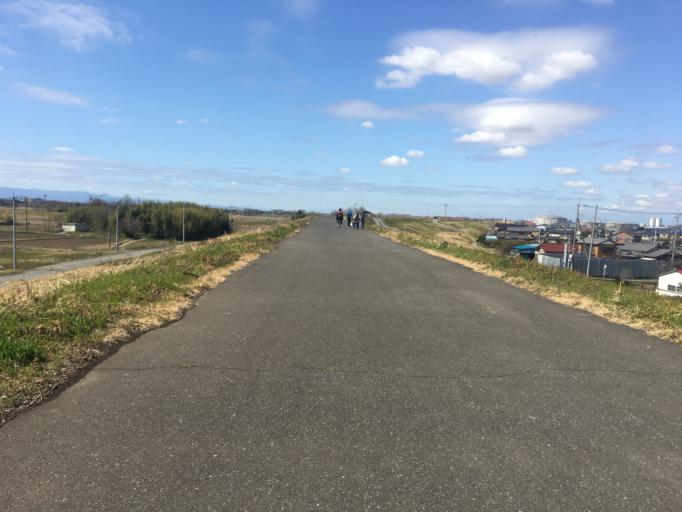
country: JP
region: Saitama
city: Shiki
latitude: 35.8662
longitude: 139.5912
